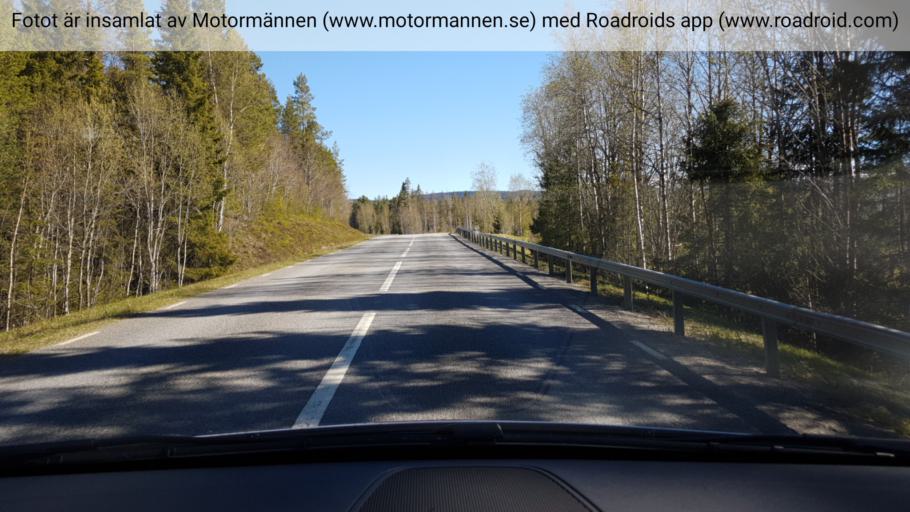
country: NO
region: Nord-Trondelag
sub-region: Lierne
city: Sandvika
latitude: 64.3938
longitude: 14.5139
